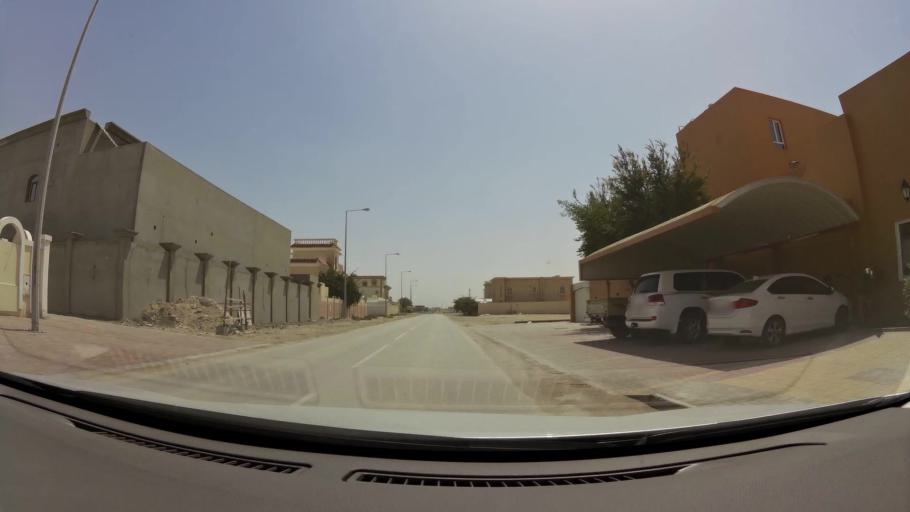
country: QA
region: Baladiyat Umm Salal
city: Umm Salal Muhammad
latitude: 25.3893
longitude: 51.4530
